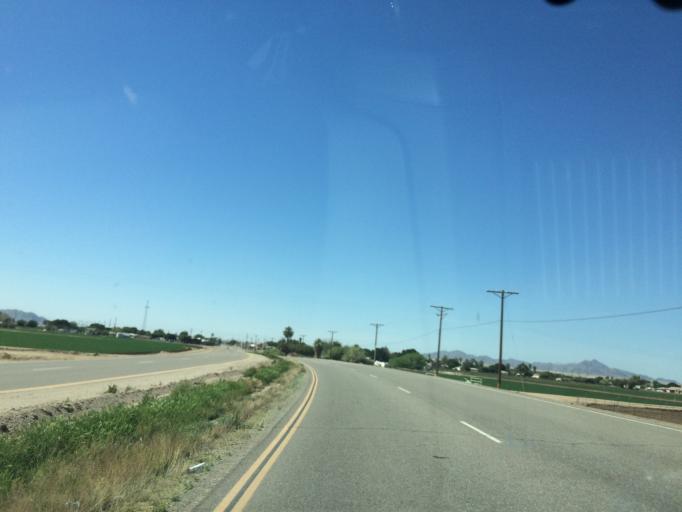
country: US
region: Arizona
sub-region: Yuma County
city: Yuma
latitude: 32.7368
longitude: -114.6280
